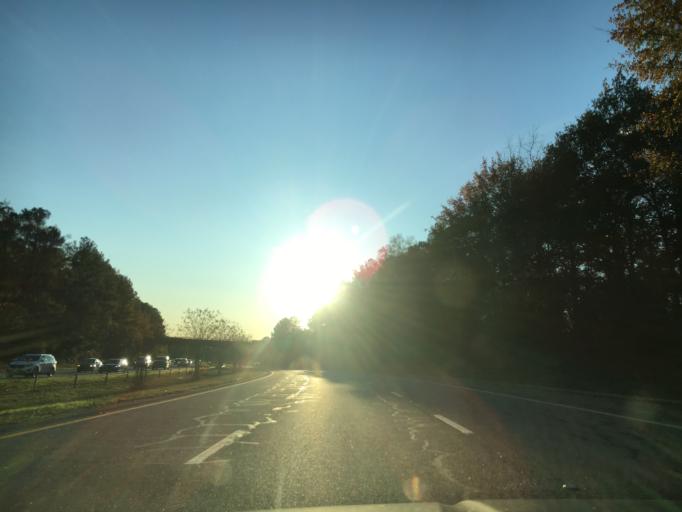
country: US
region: South Carolina
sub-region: Richland County
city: Columbia
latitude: 34.0337
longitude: -81.0299
